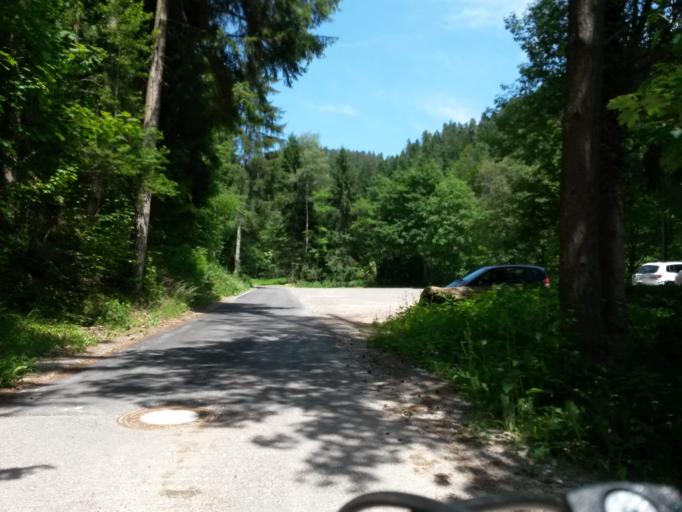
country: DE
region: Baden-Wuerttemberg
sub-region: Karlsruhe Region
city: Neubulach
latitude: 48.6585
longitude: 8.7261
